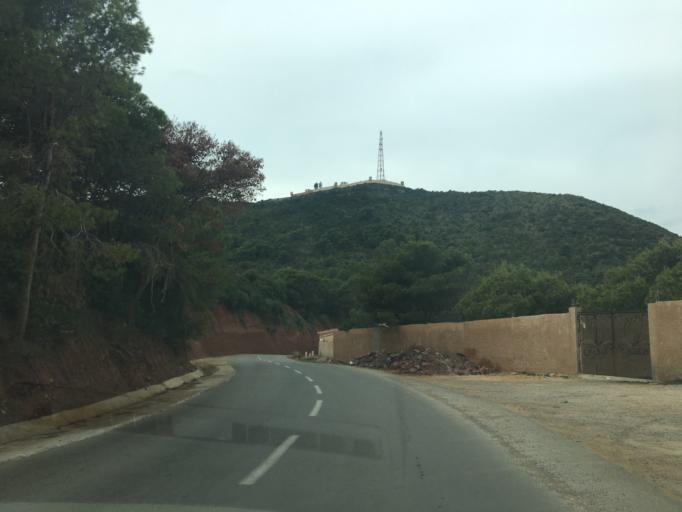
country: DZ
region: Tipaza
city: Tipasa
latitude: 36.6271
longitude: 2.4023
